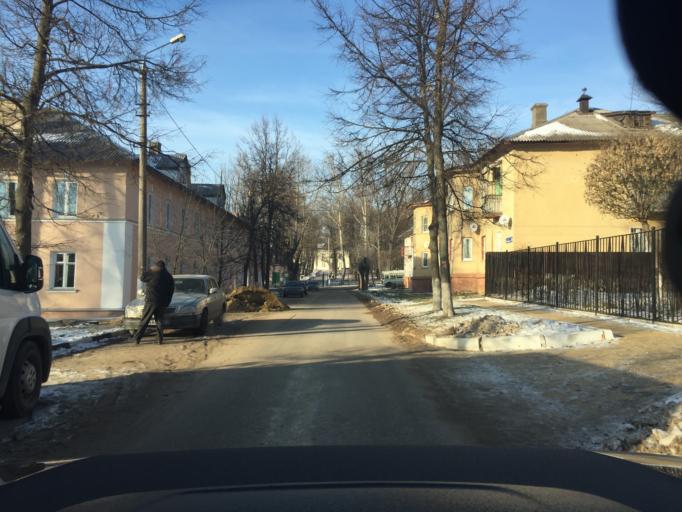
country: RU
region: Tula
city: Tula
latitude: 54.1831
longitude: 37.7038
